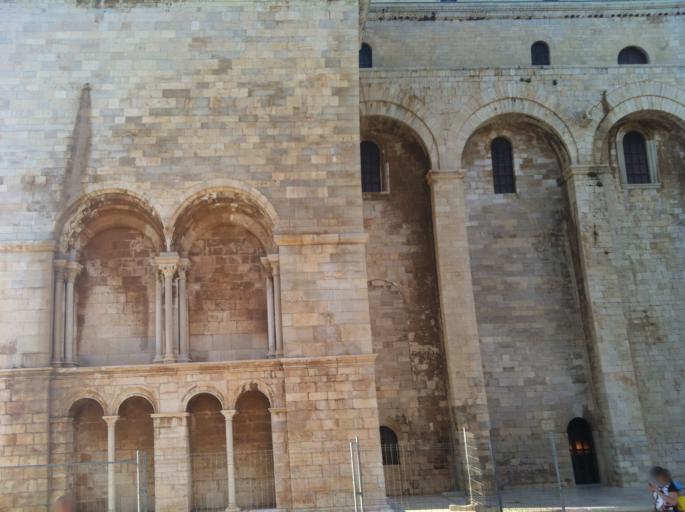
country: IT
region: Apulia
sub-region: Provincia di Barletta - Andria - Trani
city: Trani
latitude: 41.2819
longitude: 16.4184
